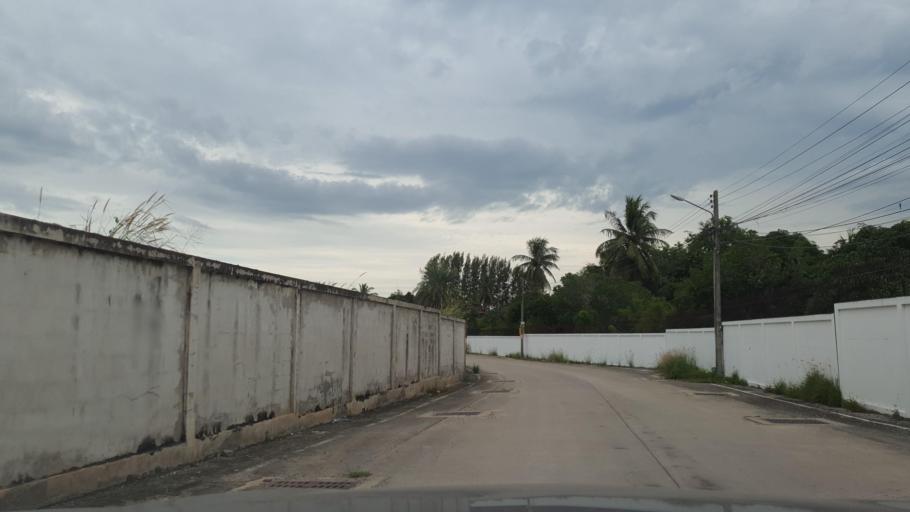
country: TH
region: Chon Buri
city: Phatthaya
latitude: 12.8785
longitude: 100.9037
